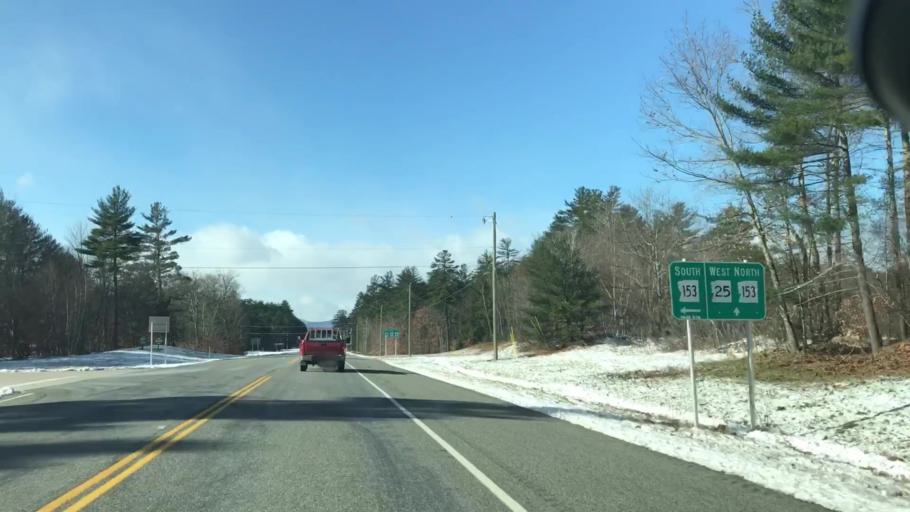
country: US
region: New Hampshire
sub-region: Carroll County
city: Freedom
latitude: 43.7924
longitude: -71.0345
